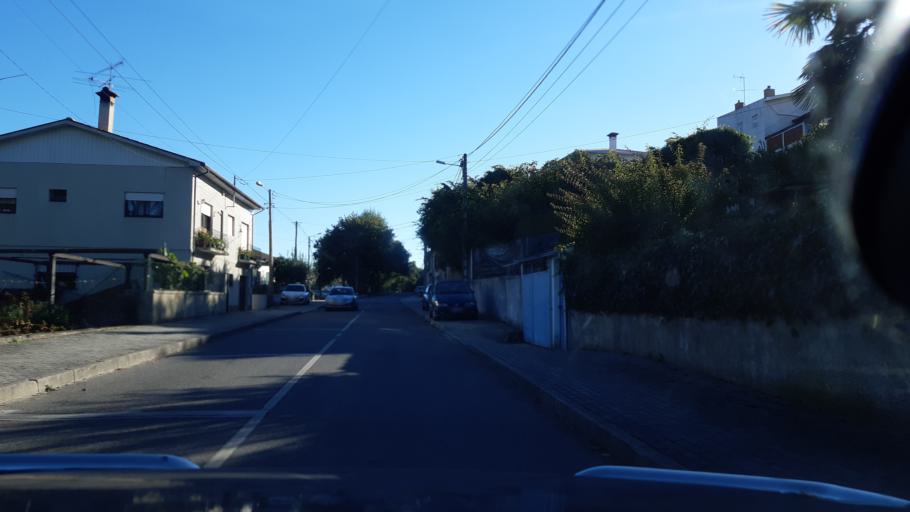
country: PT
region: Aveiro
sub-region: Agueda
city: Agueda
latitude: 40.5576
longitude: -8.4408
